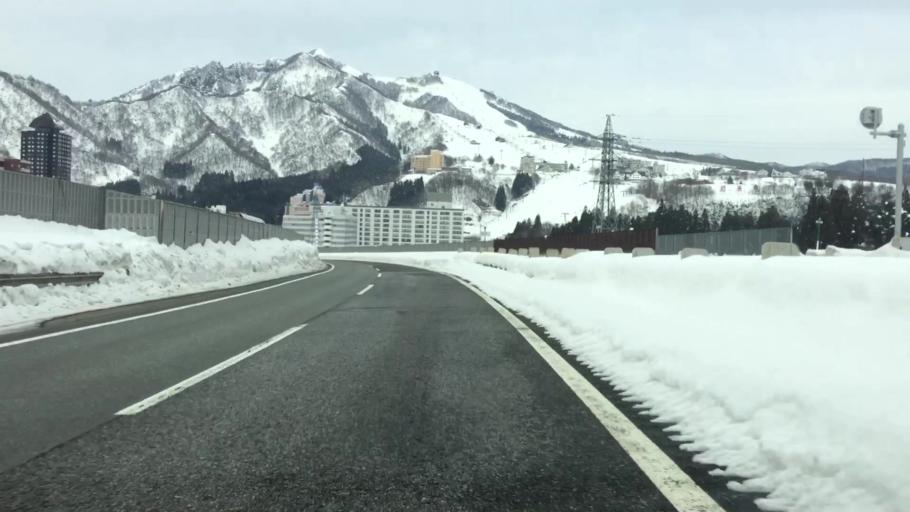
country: JP
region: Niigata
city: Shiozawa
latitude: 36.9242
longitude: 138.8415
